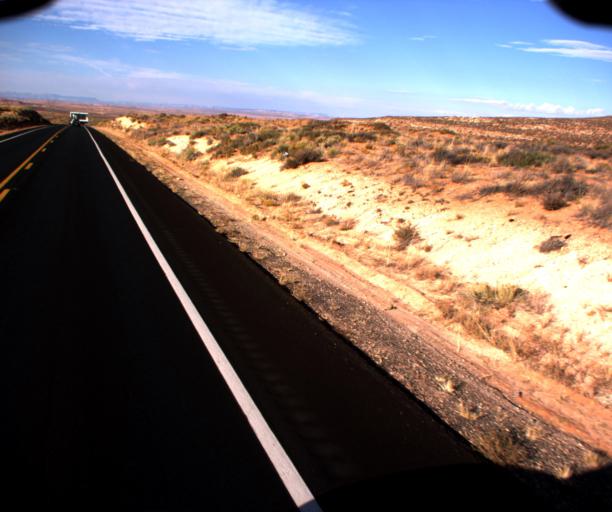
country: US
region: Arizona
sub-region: Apache County
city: Many Farms
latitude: 36.9479
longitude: -109.5256
